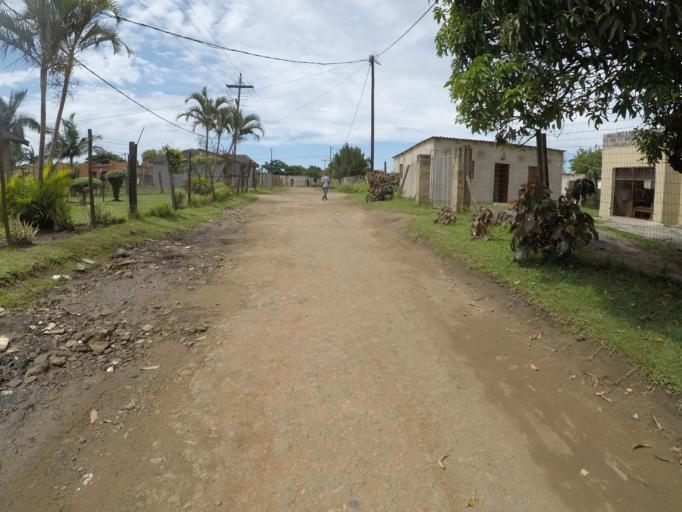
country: ZA
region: KwaZulu-Natal
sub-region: uThungulu District Municipality
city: eSikhawini
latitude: -28.8584
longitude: 31.9279
